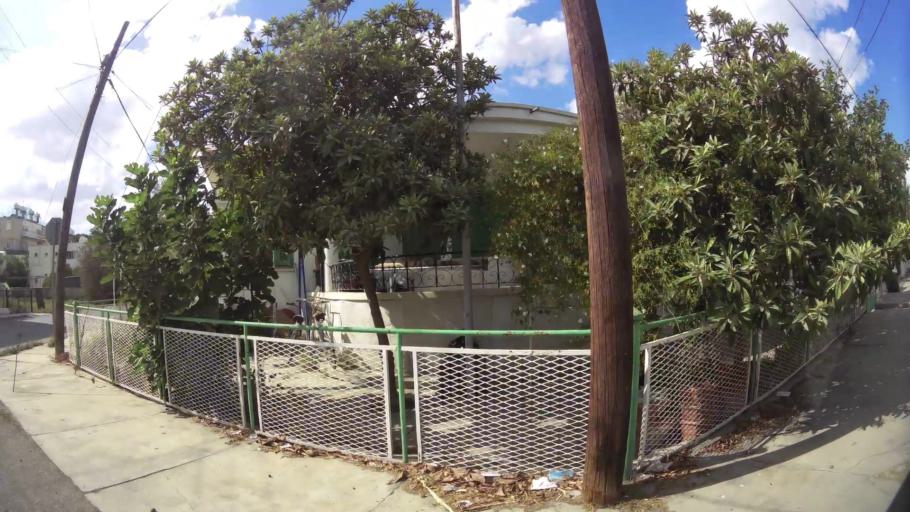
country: CY
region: Lefkosia
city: Nicosia
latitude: 35.1834
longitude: 33.3707
